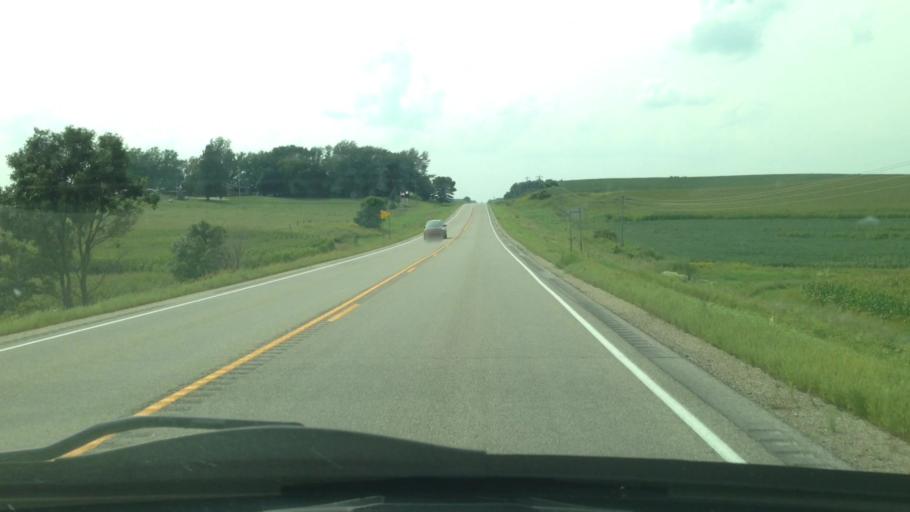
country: US
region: Minnesota
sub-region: Wabasha County
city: Elgin
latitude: 44.1653
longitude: -92.2203
